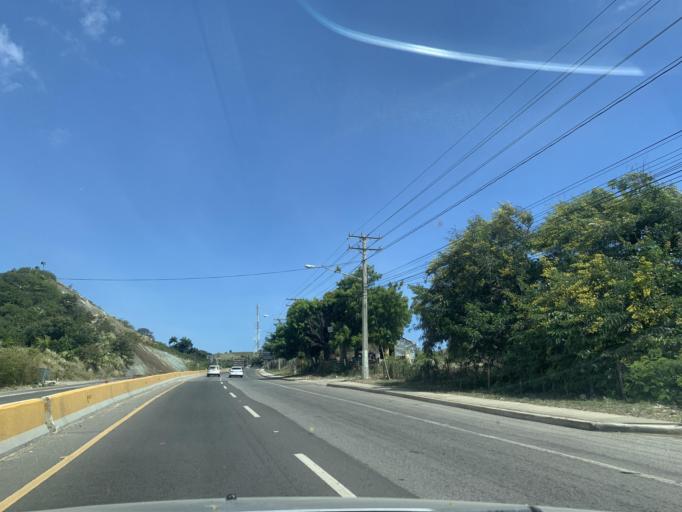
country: DO
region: Puerto Plata
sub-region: Puerto Plata
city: Puerto Plata
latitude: 19.8242
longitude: -70.7447
